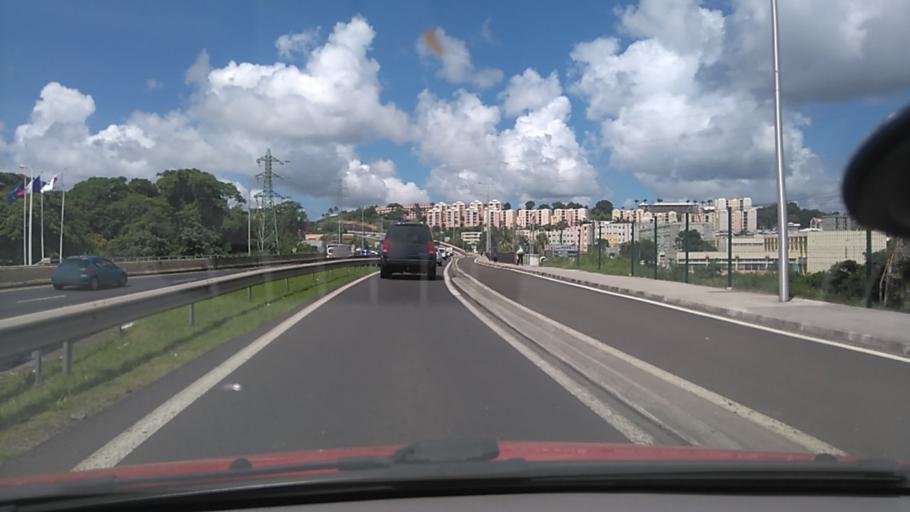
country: MQ
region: Martinique
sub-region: Martinique
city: Fort-de-France
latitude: 14.6142
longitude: -61.0503
